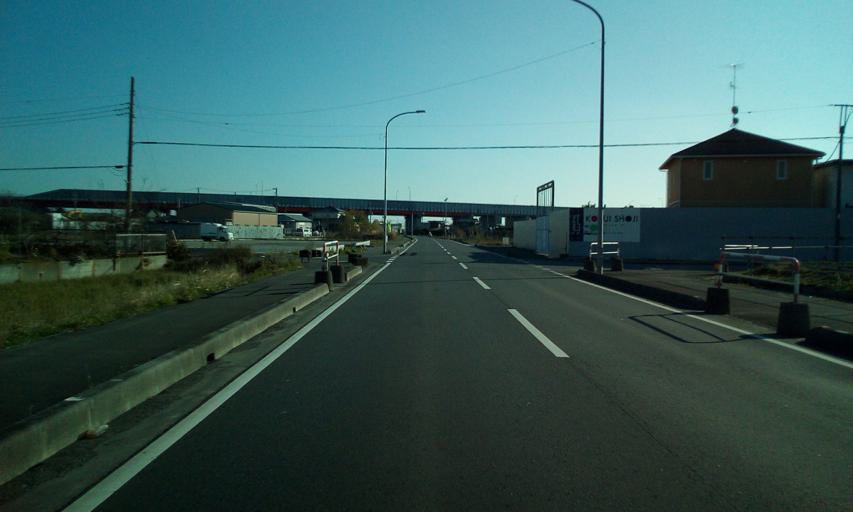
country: JP
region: Chiba
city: Nagareyama
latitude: 35.8763
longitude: 139.8886
